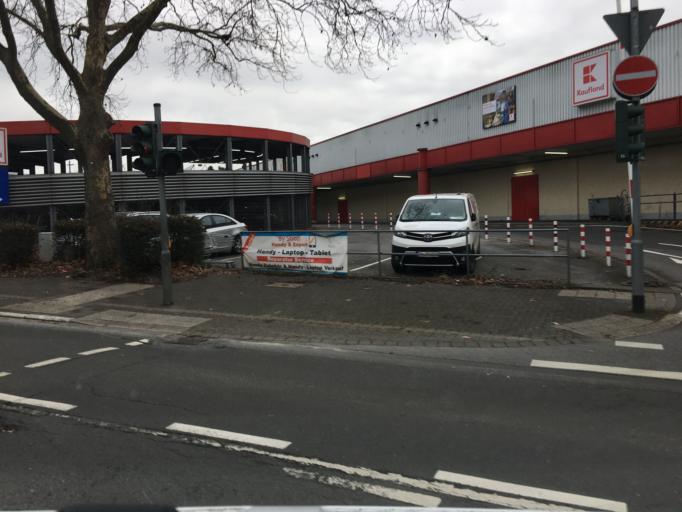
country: DE
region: North Rhine-Westphalia
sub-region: Regierungsbezirk Koln
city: Bergisch Gladbach
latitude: 50.9832
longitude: 7.1221
